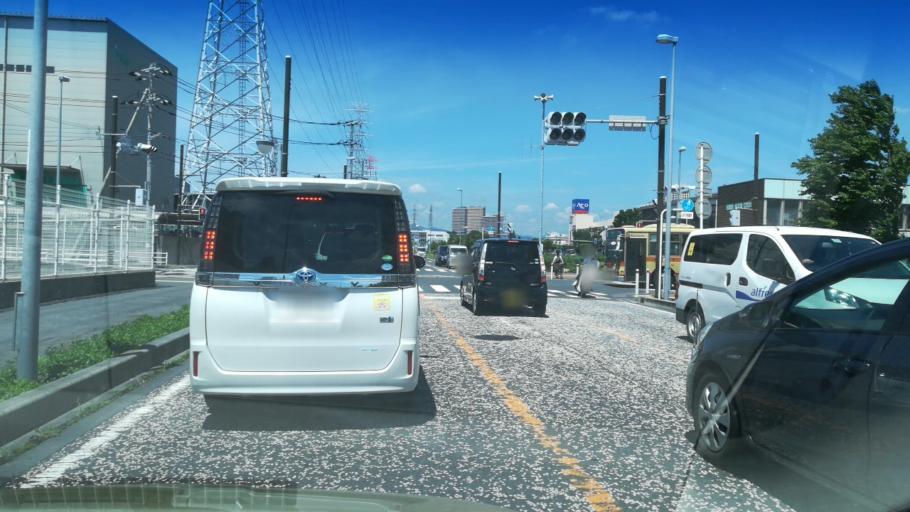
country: JP
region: Tokyo
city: Hachioji
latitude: 35.5887
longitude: 139.3515
